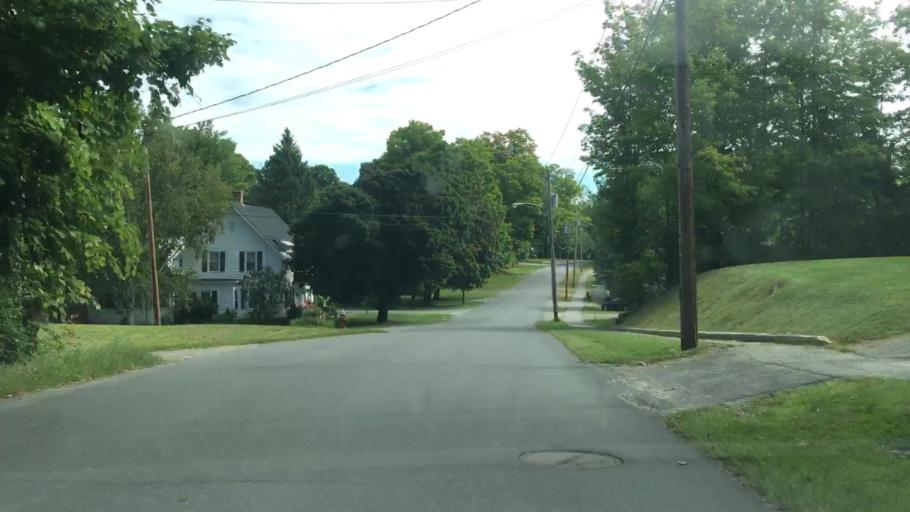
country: US
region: Maine
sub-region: Piscataquis County
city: Dover-Foxcroft
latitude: 45.1855
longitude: -69.2260
